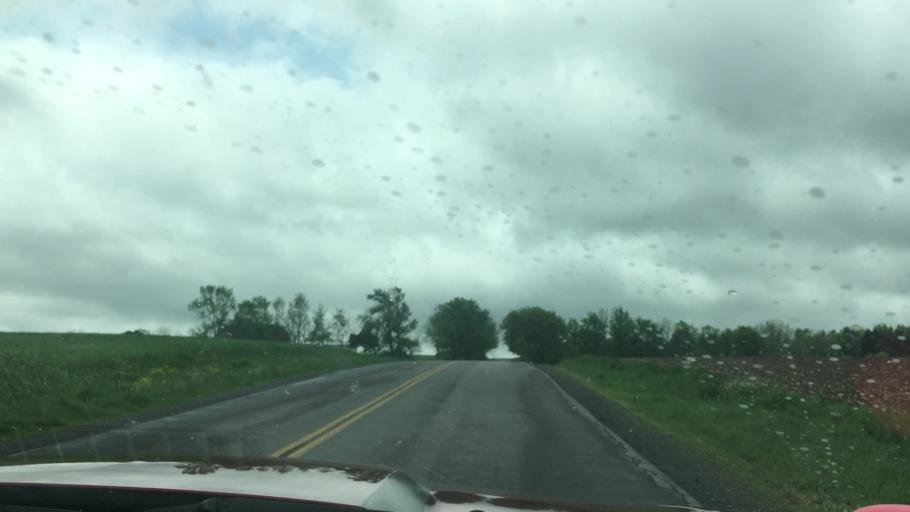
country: US
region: New York
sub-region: Genesee County
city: Batavia
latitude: 43.0875
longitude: -78.1392
